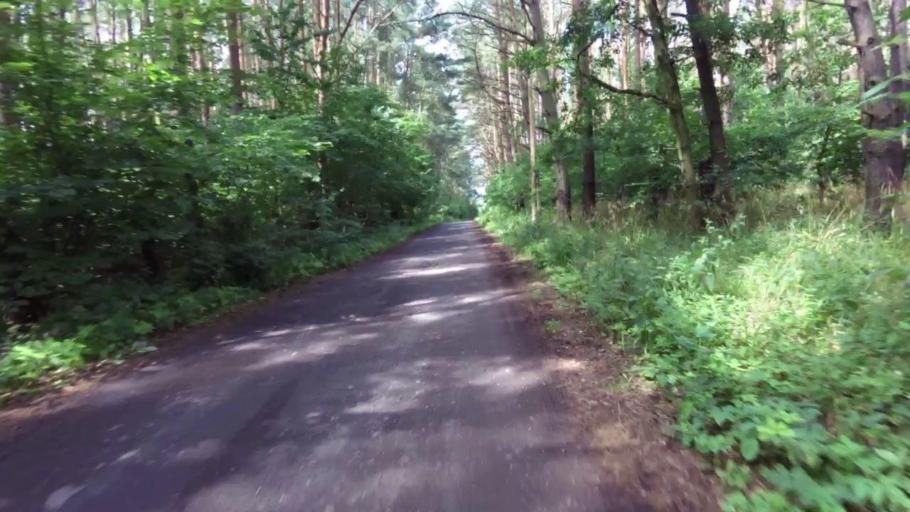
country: PL
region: West Pomeranian Voivodeship
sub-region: Powiat gryfinski
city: Stare Czarnowo
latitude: 53.3578
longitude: 14.7297
